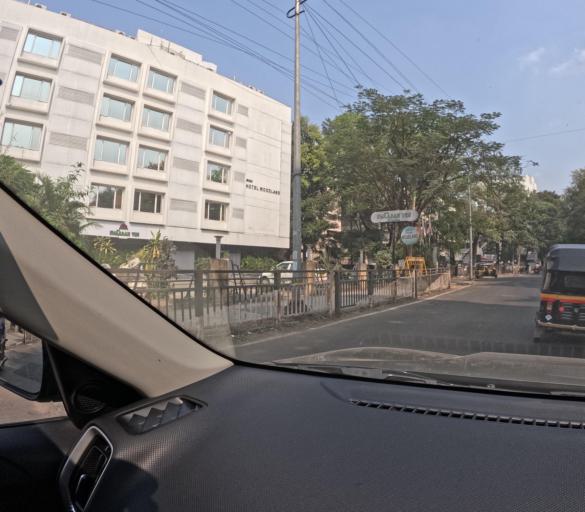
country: IN
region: Maharashtra
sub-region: Pune Division
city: Pune
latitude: 18.5249
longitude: 73.8753
